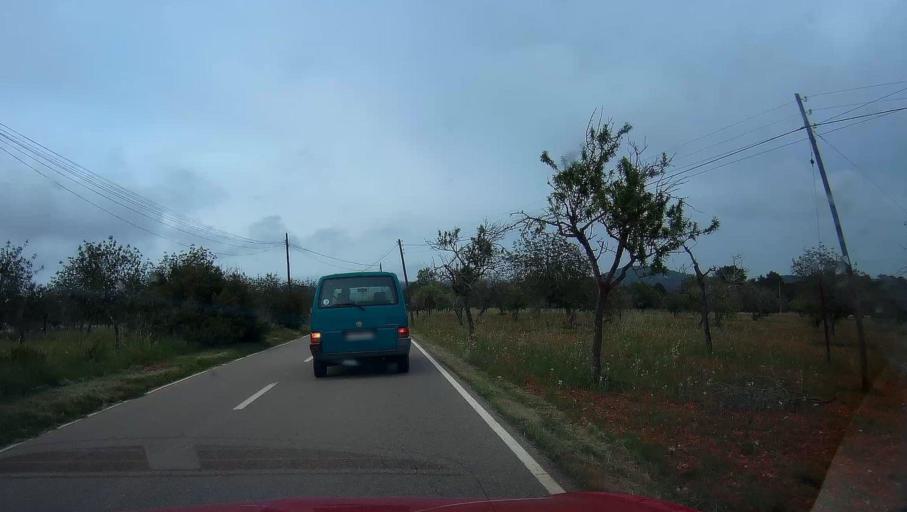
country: ES
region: Balearic Islands
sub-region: Illes Balears
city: Sant Joan de Labritja
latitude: 39.0460
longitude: 1.4123
